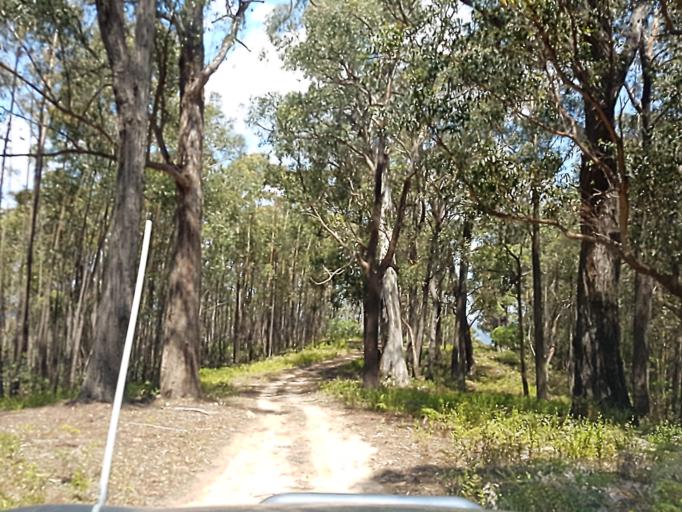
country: AU
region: Victoria
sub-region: East Gippsland
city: Lakes Entrance
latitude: -37.3964
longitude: 148.2975
